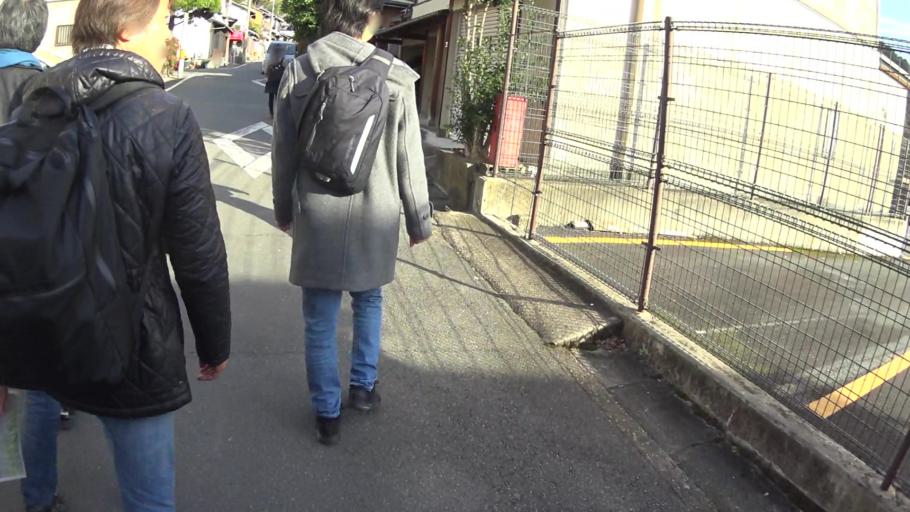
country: JP
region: Kyoto
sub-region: Kyoto-shi
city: Kamigyo-ku
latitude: 35.0155
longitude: 135.7939
